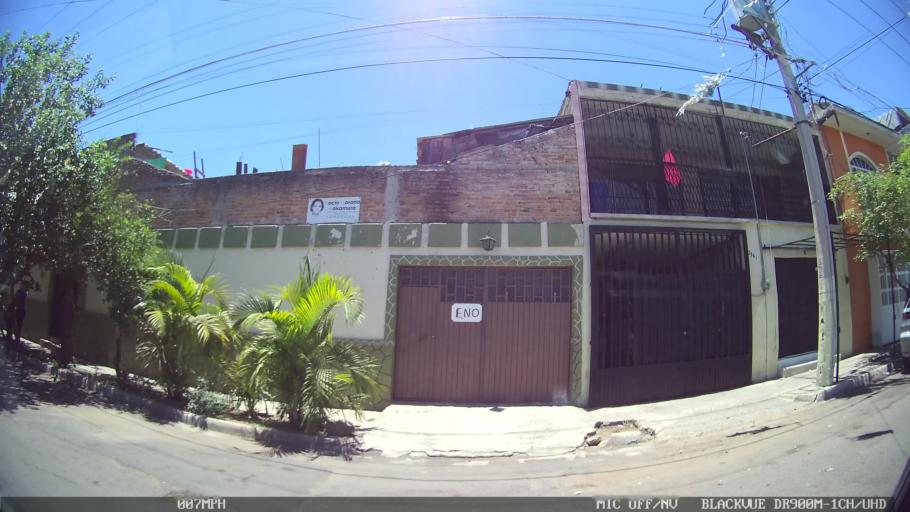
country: MX
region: Jalisco
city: Tlaquepaque
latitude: 20.6678
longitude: -103.2958
